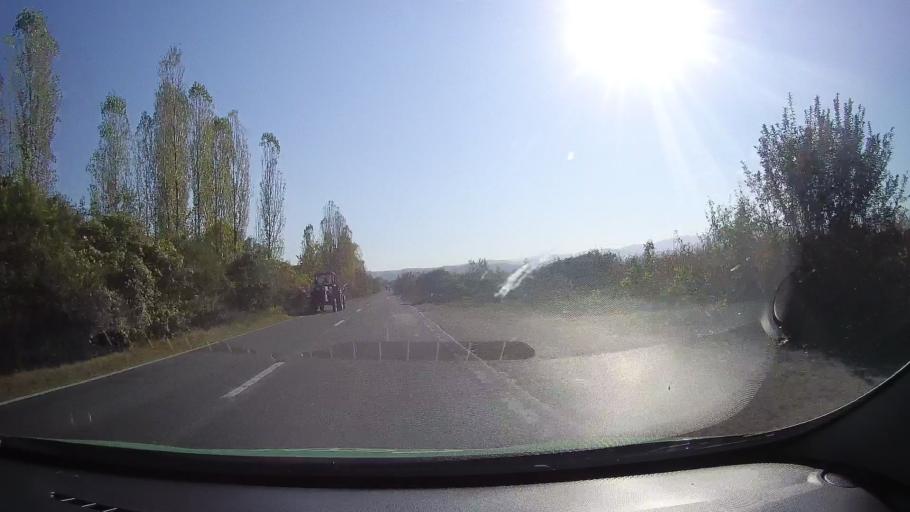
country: RO
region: Timis
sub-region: Comuna Margina
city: Margina
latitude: 45.8507
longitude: 22.2972
